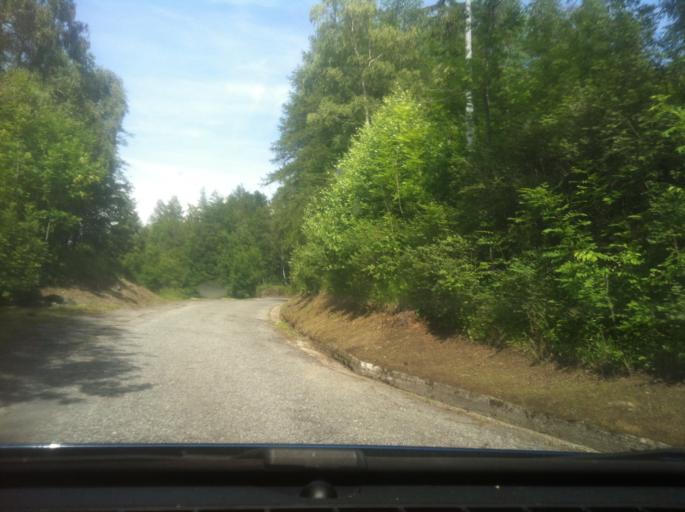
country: IT
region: Aosta Valley
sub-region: Valle d'Aosta
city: Nus
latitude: 45.7202
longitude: 7.4671
